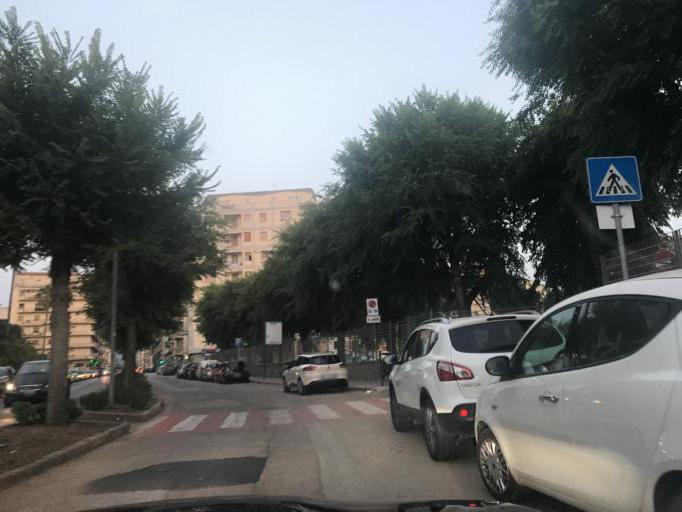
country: IT
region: Sardinia
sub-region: Provincia di Sassari
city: Alghero
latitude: 40.5559
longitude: 8.3184
